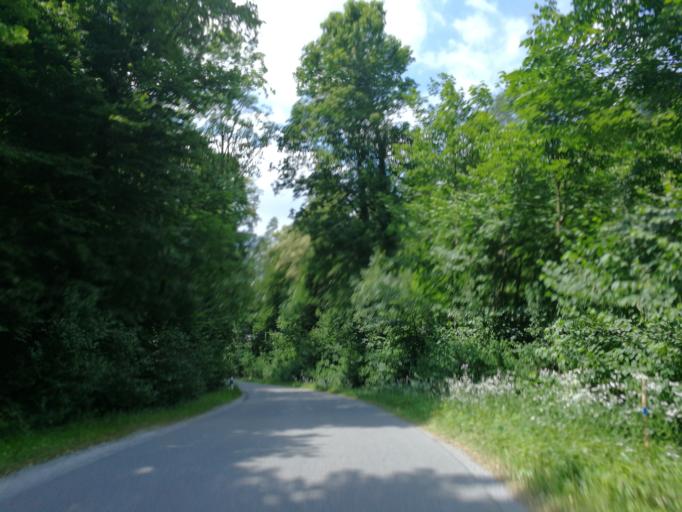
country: CH
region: Saint Gallen
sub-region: Wahlkreis See-Gaster
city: Benken
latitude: 47.1767
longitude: 9.0060
